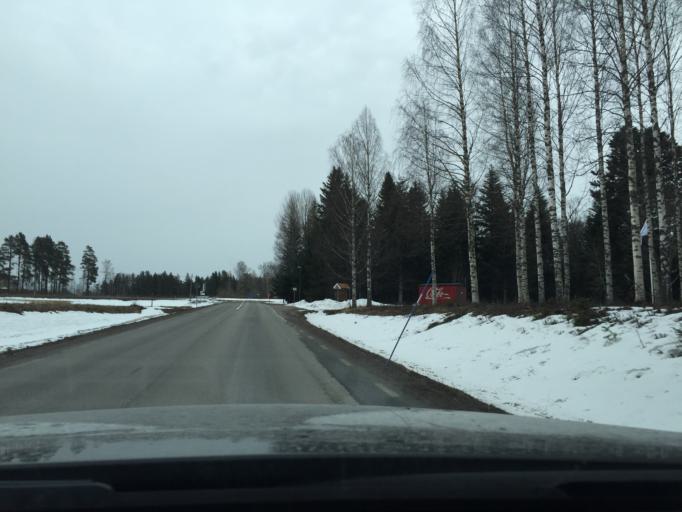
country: SE
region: Gaevleborg
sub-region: Sandvikens Kommun
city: Jarbo
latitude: 60.7599
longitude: 16.5326
